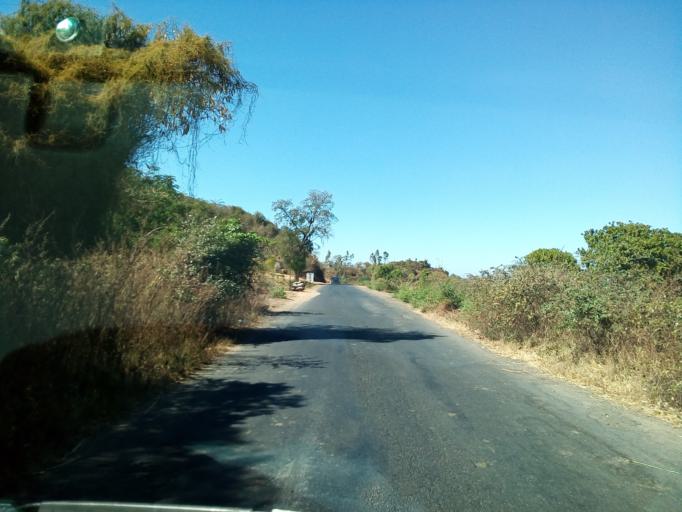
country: MG
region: Boeny
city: Ambato Boeny
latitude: -16.3664
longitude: 46.9062
